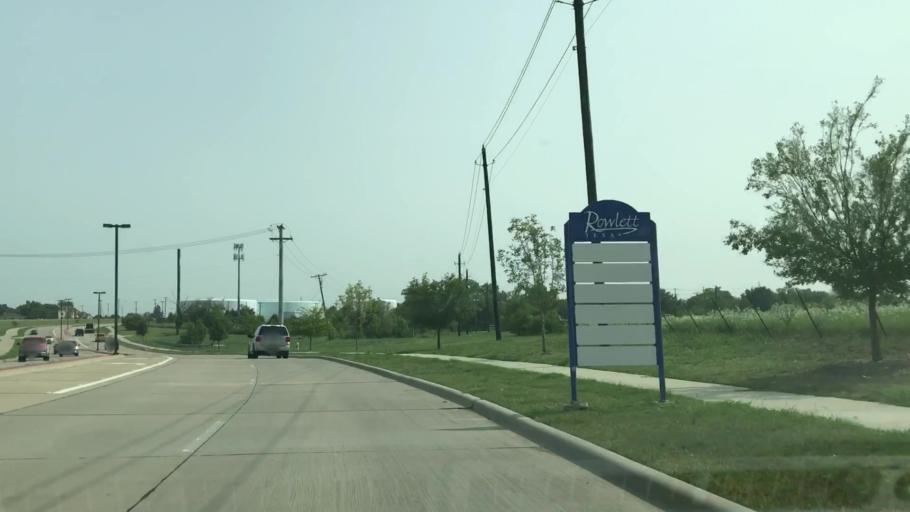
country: US
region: Texas
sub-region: Dallas County
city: Sachse
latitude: 32.9471
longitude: -96.5708
